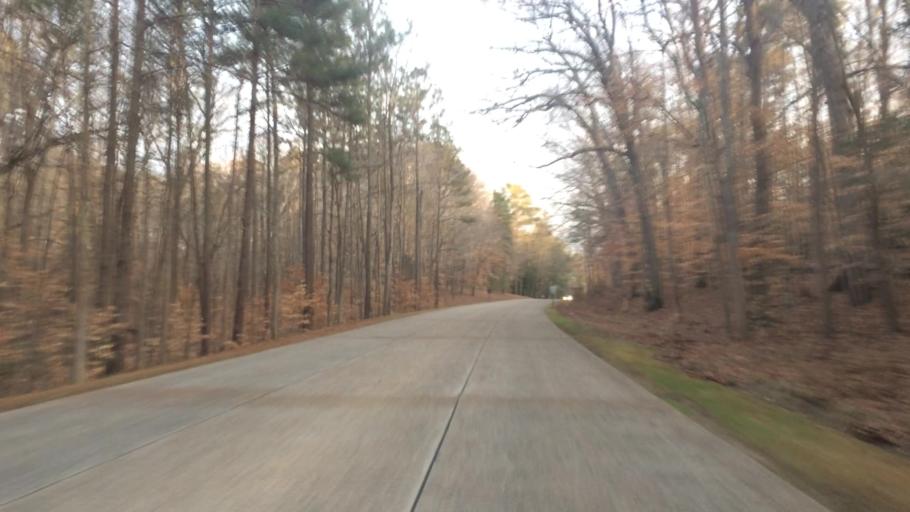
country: US
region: Virginia
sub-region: City of Williamsburg
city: Williamsburg
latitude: 37.2520
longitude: -76.7021
